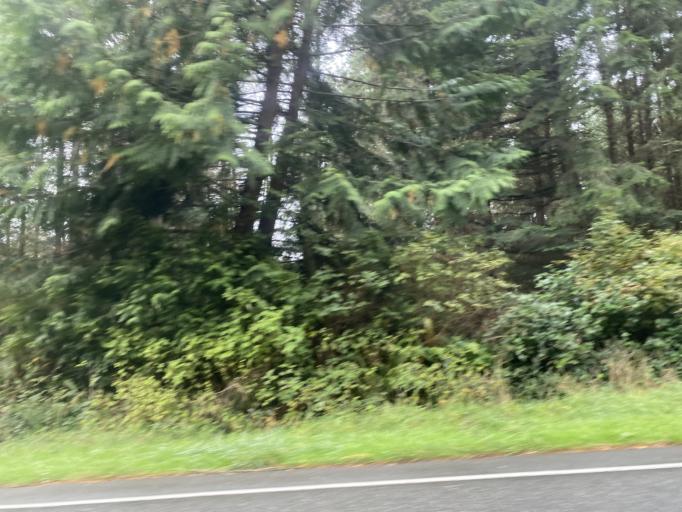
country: US
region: Washington
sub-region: Island County
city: Freeland
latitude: 48.0616
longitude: -122.5067
